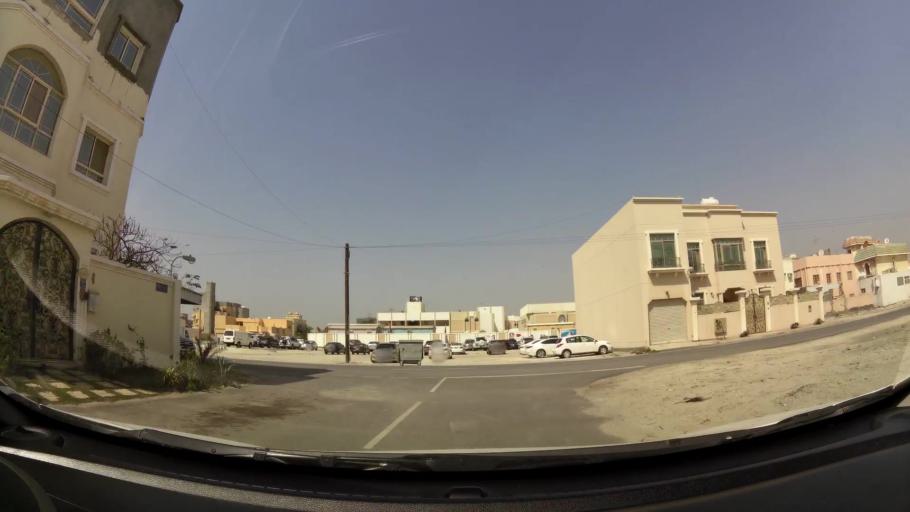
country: BH
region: Manama
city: Jidd Hafs
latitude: 26.2087
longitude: 50.4482
